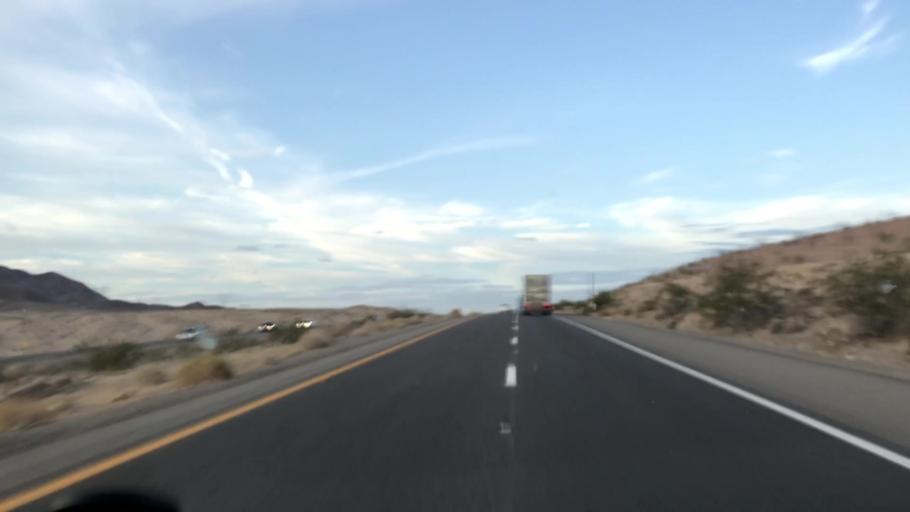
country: US
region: California
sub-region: San Bernardino County
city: Fort Irwin
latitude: 35.1180
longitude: -116.2353
